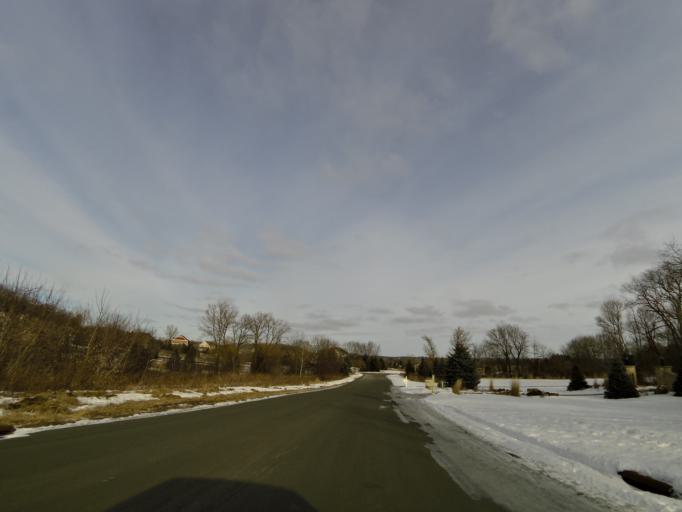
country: US
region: Minnesota
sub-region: Washington County
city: Lakeland
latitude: 44.9809
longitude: -92.7982
